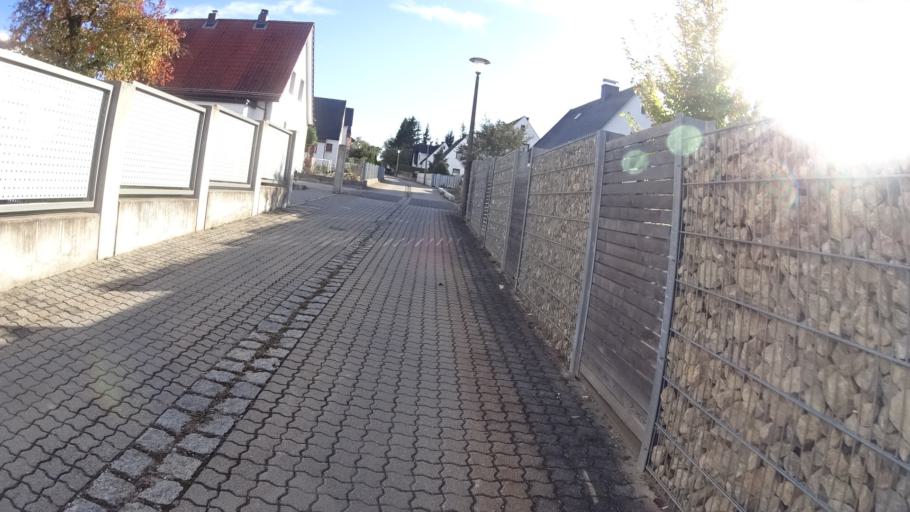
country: DE
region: Bavaria
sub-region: Upper Bavaria
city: Bohmfeld
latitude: 48.8628
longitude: 11.3622
